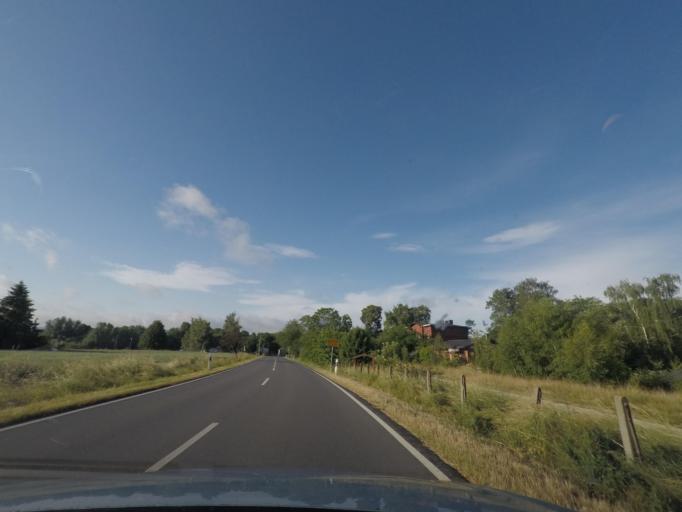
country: DE
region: Saxony-Anhalt
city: Huy-Neinstedt
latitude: 51.9911
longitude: 10.8935
